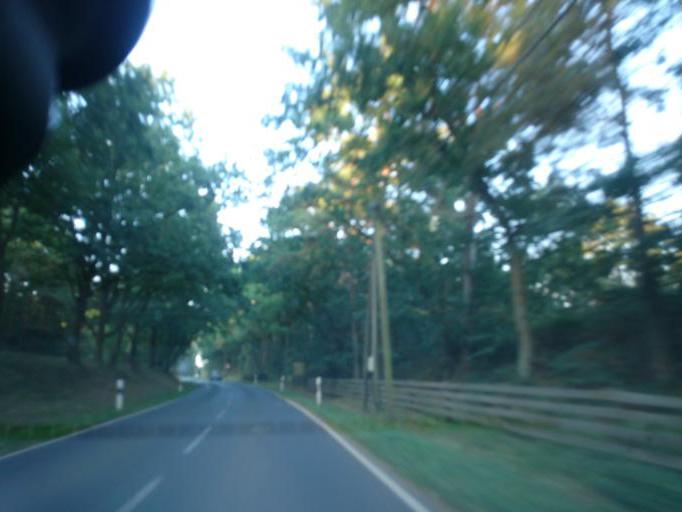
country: DE
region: Mecklenburg-Vorpommern
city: Born
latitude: 54.3535
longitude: 12.5917
